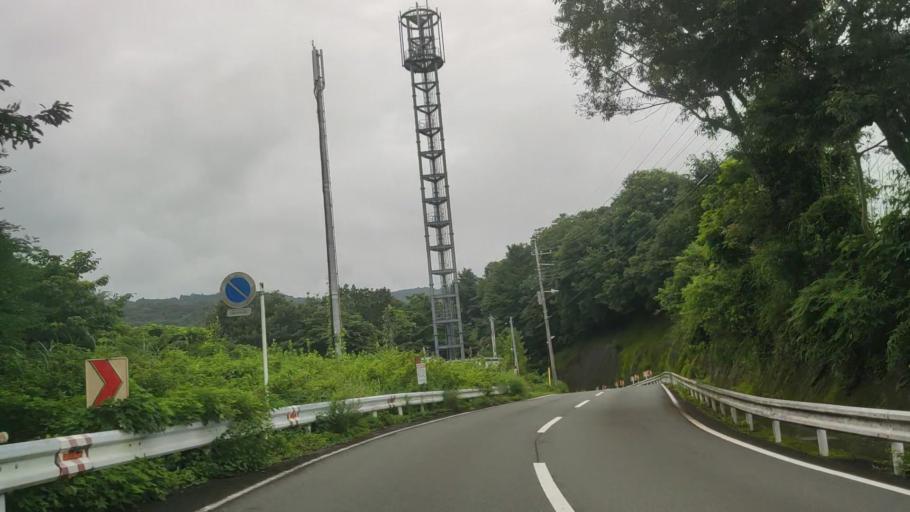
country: JP
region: Shizuoka
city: Fujinomiya
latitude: 35.2100
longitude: 138.5892
